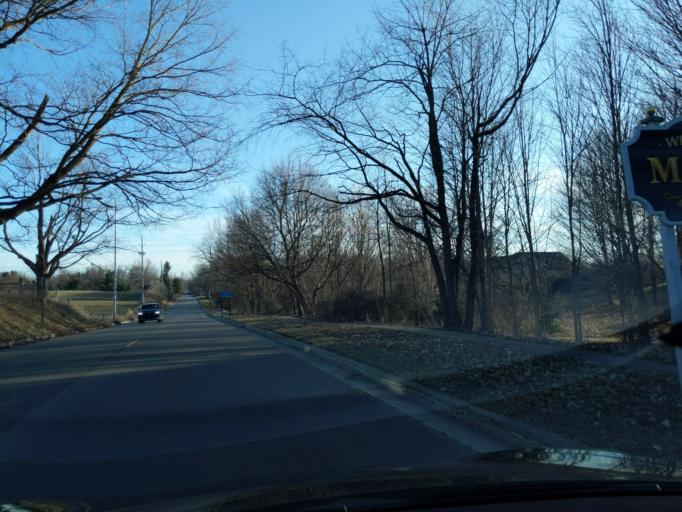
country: US
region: Michigan
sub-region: Ingham County
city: Mason
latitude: 42.5926
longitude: -84.4432
